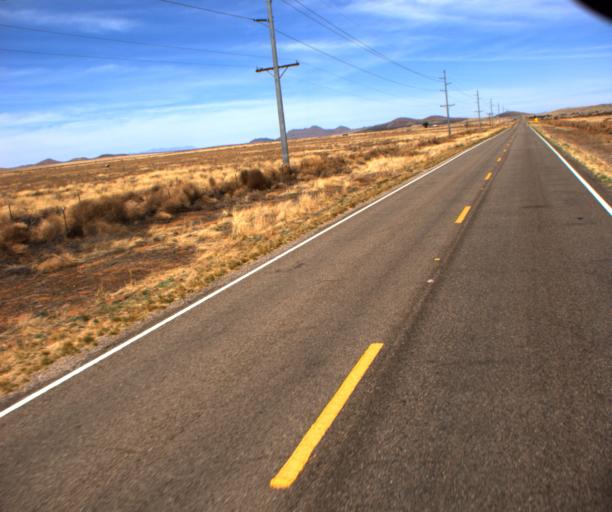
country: US
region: Arizona
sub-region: Cochise County
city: Tombstone
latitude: 31.8497
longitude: -109.6952
